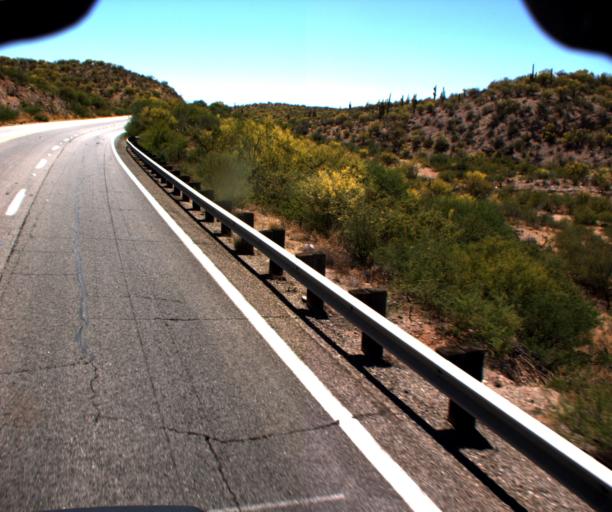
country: US
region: Arizona
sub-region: Pinal County
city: Mammoth
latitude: 32.6718
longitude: -110.6650
